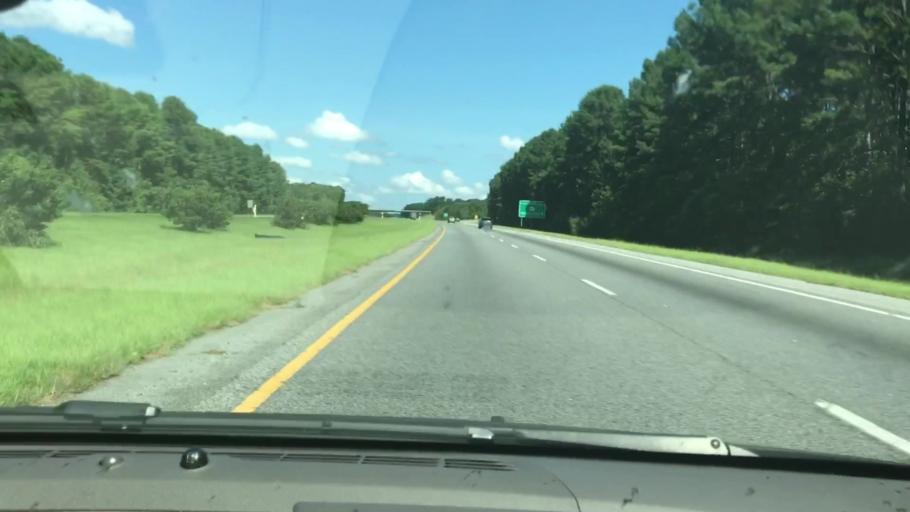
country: US
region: Georgia
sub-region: Harris County
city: Hamilton
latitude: 32.6565
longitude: -84.9755
